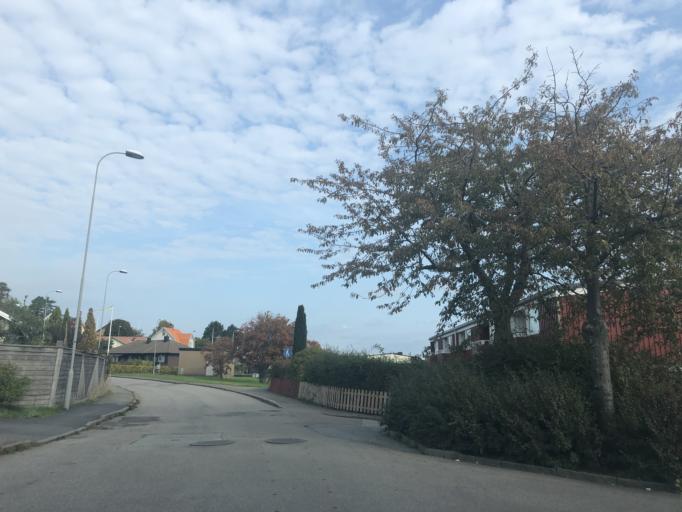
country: SE
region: Vaestra Goetaland
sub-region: Goteborg
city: Majorna
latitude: 57.6534
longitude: 11.8669
